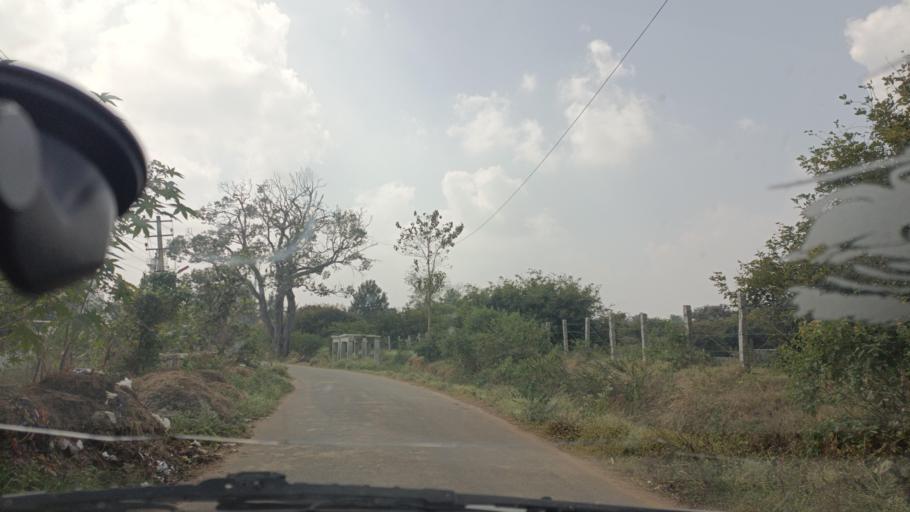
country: IN
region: Karnataka
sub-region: Bangalore Urban
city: Yelahanka
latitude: 13.1525
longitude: 77.6389
